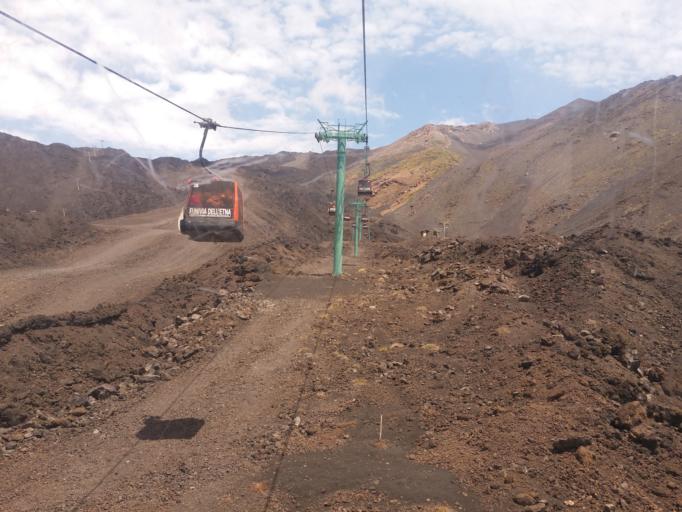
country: IT
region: Sicily
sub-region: Catania
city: Ragalna
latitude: 37.7060
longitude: 14.9993
